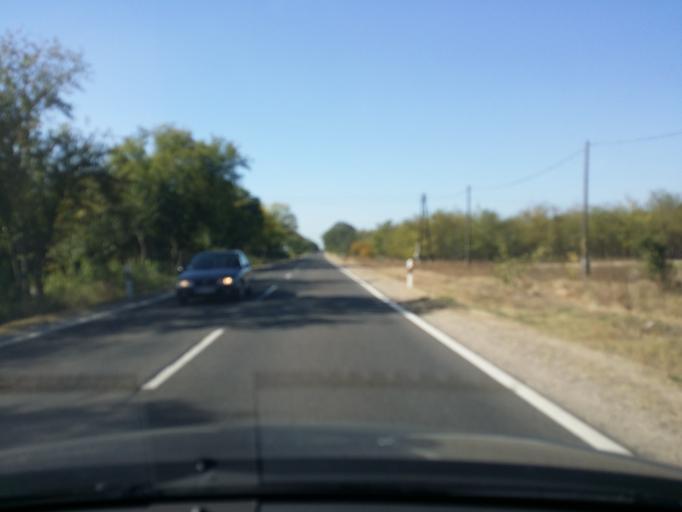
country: HU
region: Bacs-Kiskun
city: Nyarlorinc
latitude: 46.8641
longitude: 19.9156
